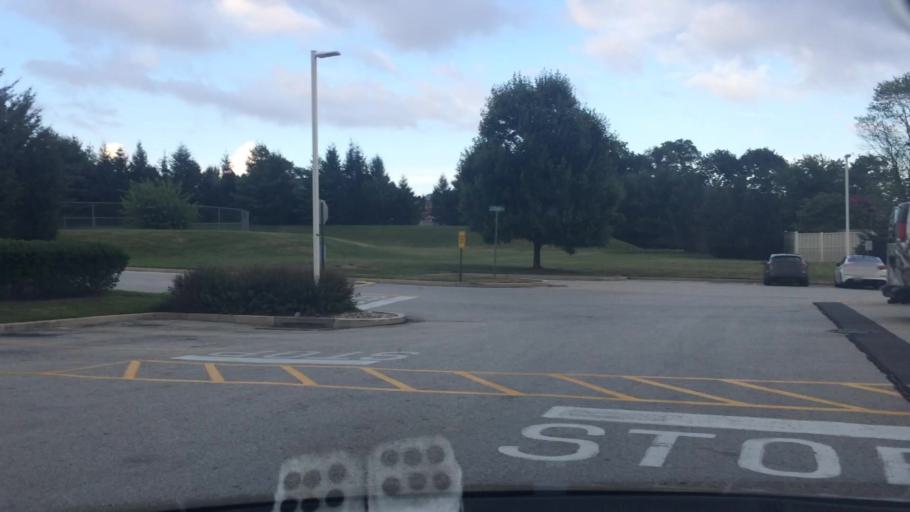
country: US
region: Pennsylvania
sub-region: Delaware County
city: Village Green-Green Ridge
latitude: 39.8656
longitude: -75.4274
